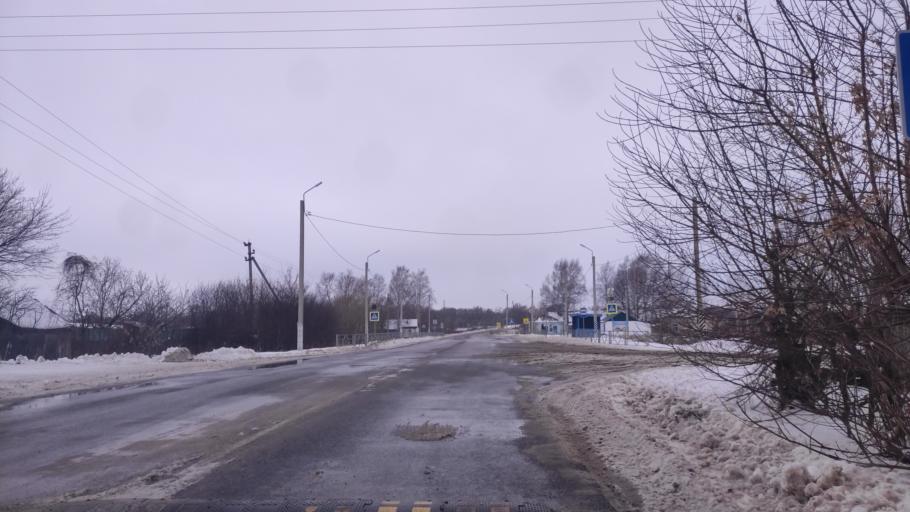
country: RU
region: Tambov
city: Pervomayskiy
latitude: 53.3038
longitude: 40.3819
